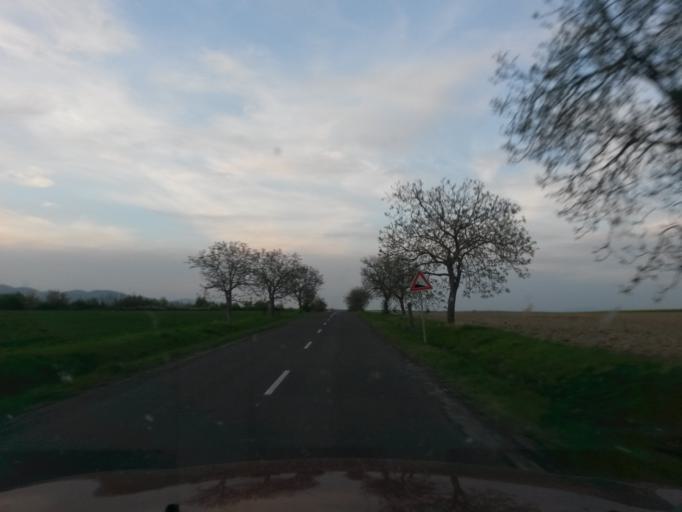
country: SK
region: Kosicky
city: Secovce
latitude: 48.5579
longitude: 21.5586
